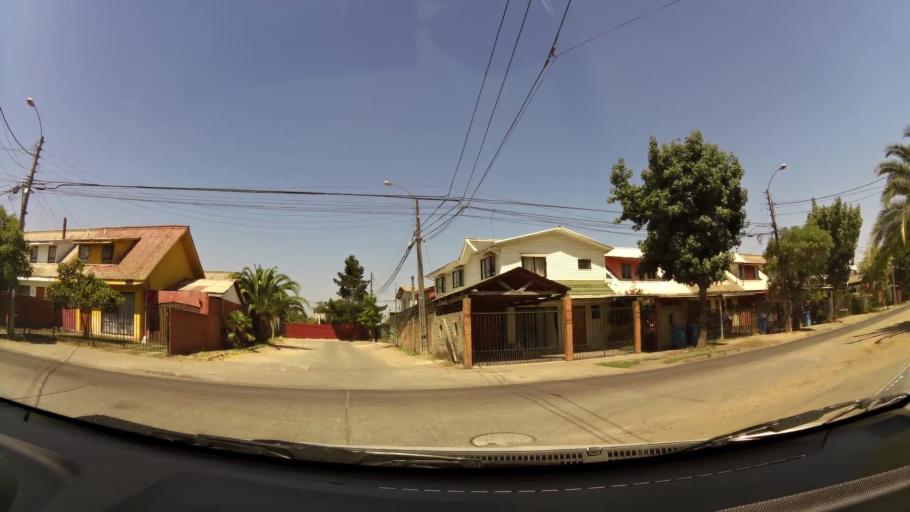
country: CL
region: Maule
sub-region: Provincia de Talca
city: Talca
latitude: -35.4224
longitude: -71.6301
